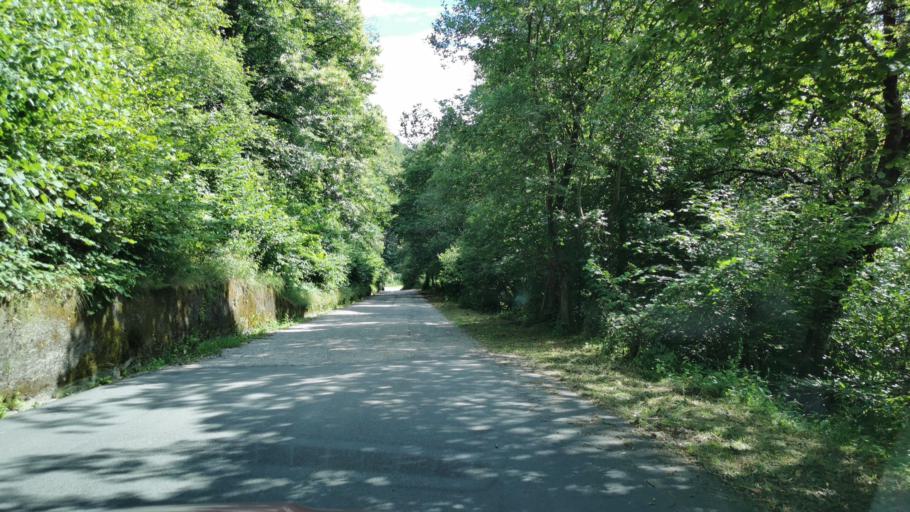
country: IT
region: Lombardy
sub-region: Provincia di Lecco
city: Casargo
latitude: 46.0398
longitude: 9.3954
